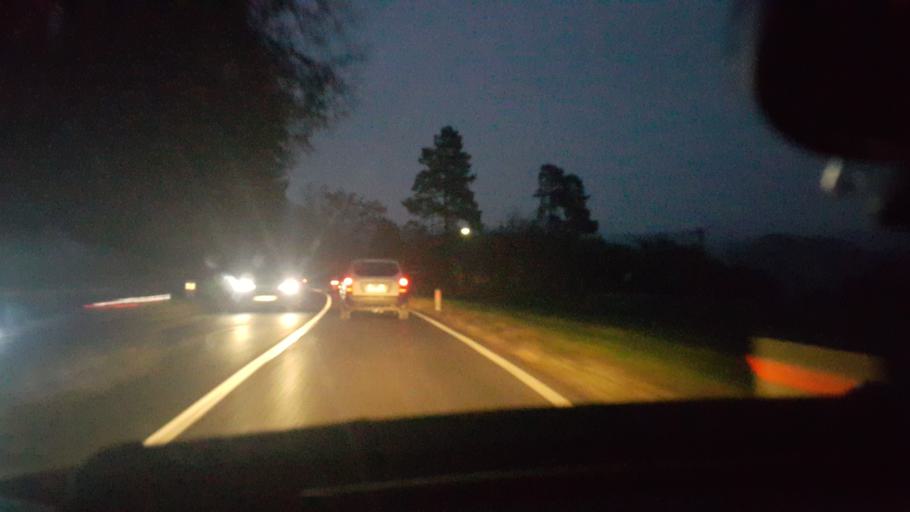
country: SI
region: Vuzenica
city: Vuzenica
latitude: 46.5983
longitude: 15.1531
